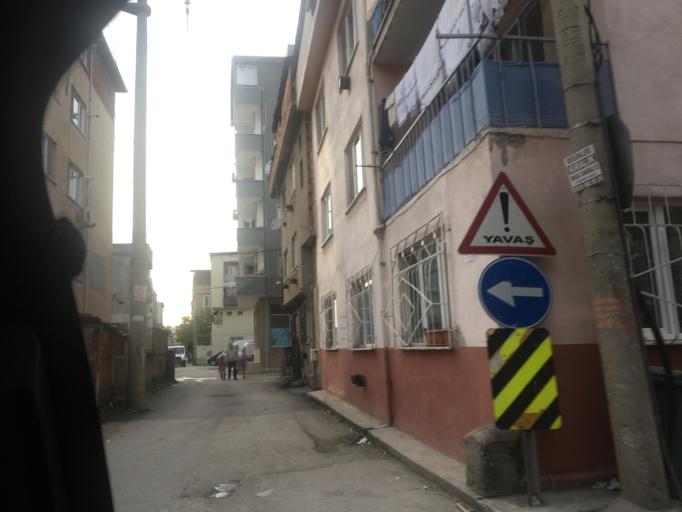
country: TR
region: Bursa
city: Yildirim
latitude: 40.2095
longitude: 29.0303
